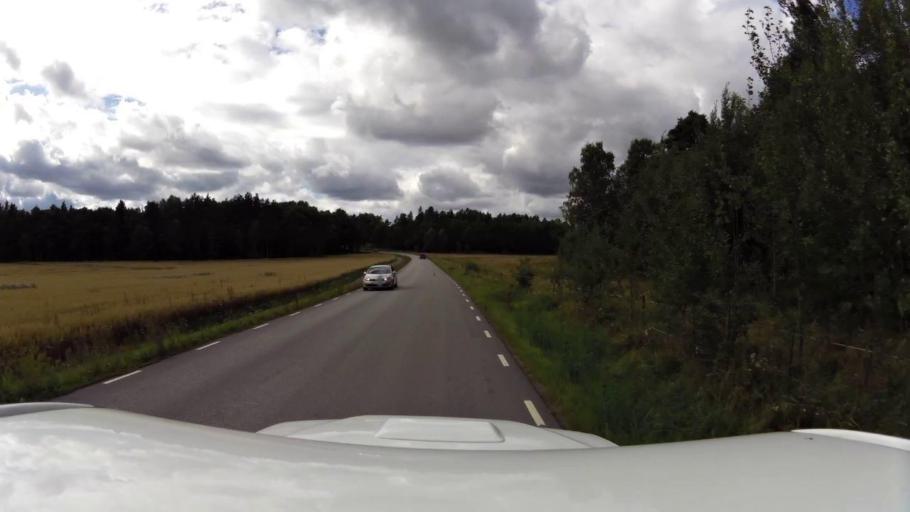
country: SE
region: OEstergoetland
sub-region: Linkopings Kommun
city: Linkoping
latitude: 58.3709
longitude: 15.5822
